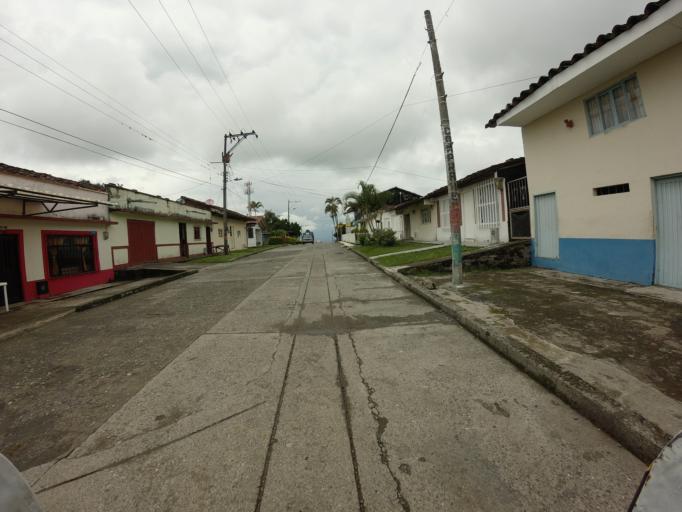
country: CO
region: Valle del Cauca
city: Ulloa
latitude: 4.7009
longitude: -75.7353
